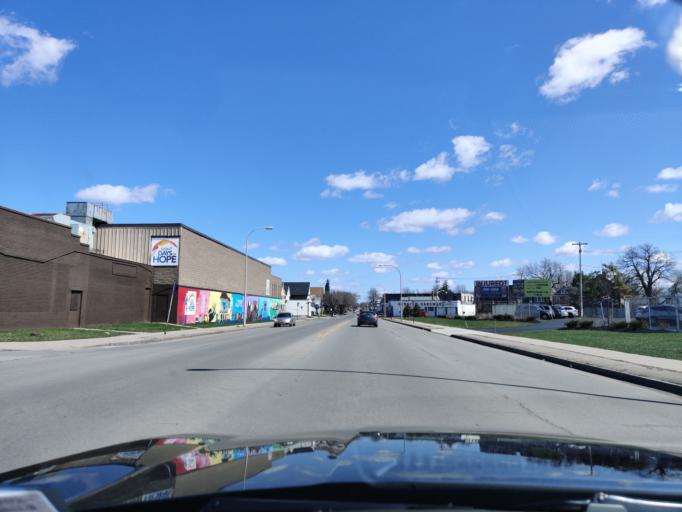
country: US
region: New York
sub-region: Erie County
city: Eggertsville
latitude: 42.9344
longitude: -78.8225
